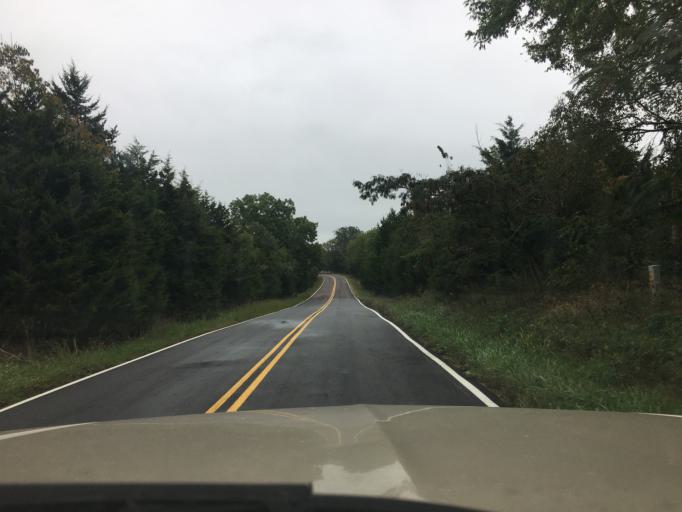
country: US
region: Missouri
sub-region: Crawford County
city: Cuba
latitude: 38.1911
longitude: -91.4738
